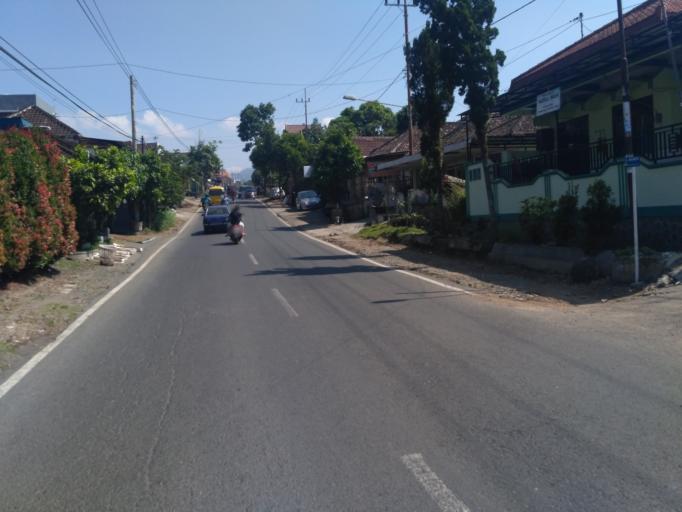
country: ID
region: East Java
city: Batu
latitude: -7.8646
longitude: 112.5387
